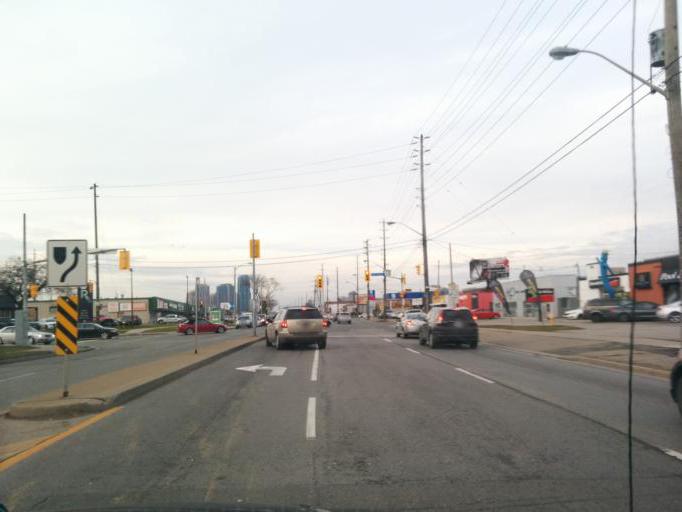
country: CA
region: Ontario
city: Etobicoke
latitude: 43.6247
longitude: -79.5283
